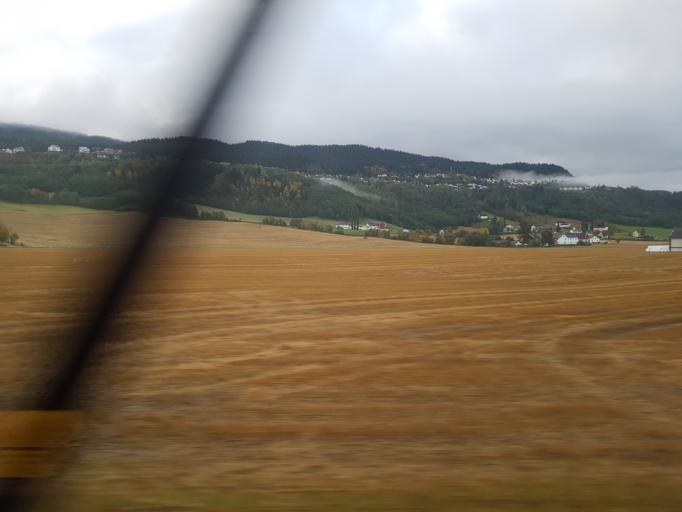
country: NO
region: Sor-Trondelag
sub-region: Melhus
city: Melhus
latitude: 63.3041
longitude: 10.2904
